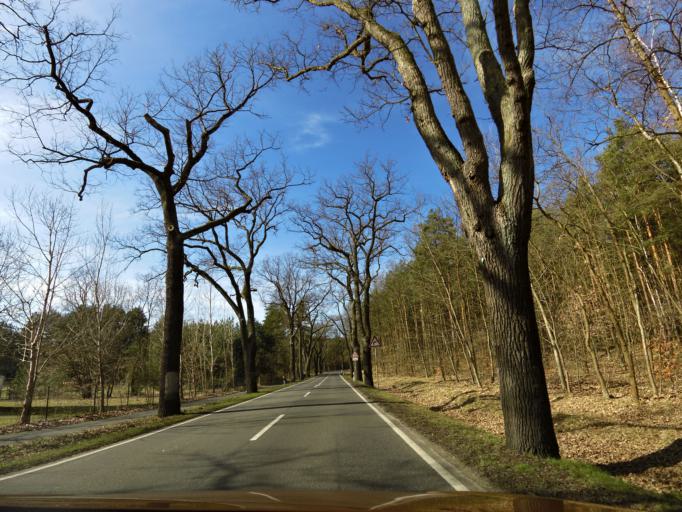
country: DE
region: Brandenburg
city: Beelitz
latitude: 52.2362
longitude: 12.9489
